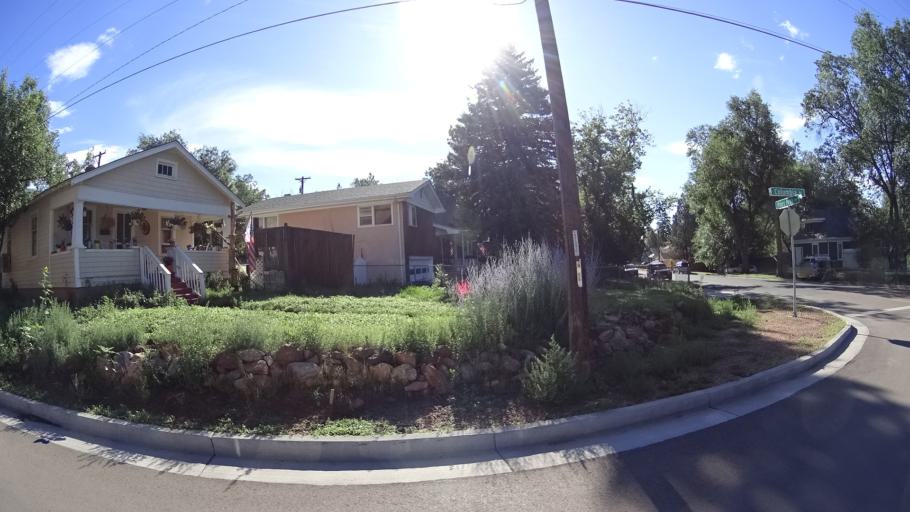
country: US
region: Colorado
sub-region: El Paso County
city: Manitou Springs
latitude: 38.8577
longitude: -104.8847
